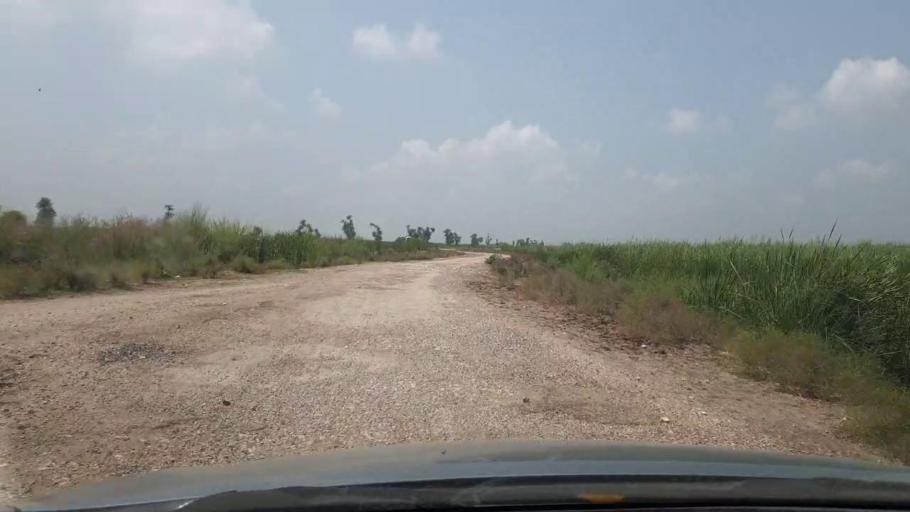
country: PK
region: Sindh
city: Khairpur
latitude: 27.4825
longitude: 68.7073
